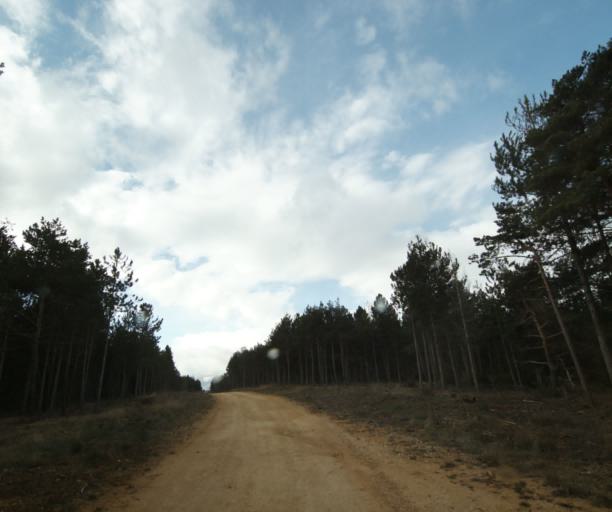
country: FR
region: Midi-Pyrenees
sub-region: Departement de l'Aveyron
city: Millau
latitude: 44.1279
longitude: 3.1527
